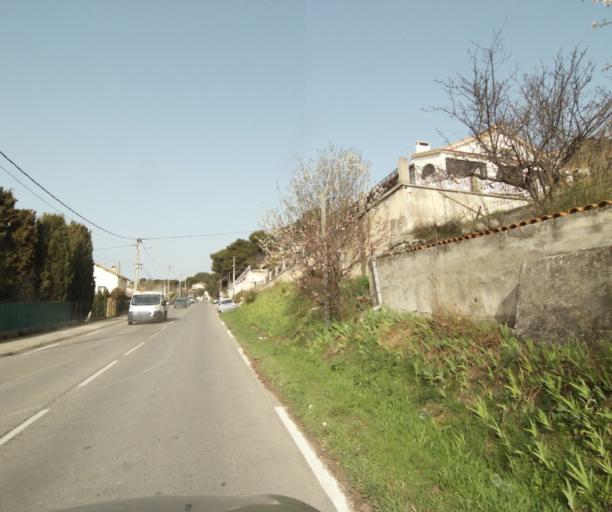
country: FR
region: Provence-Alpes-Cote d'Azur
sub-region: Departement des Bouches-du-Rhone
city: Marseille 15
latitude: 43.3916
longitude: 5.3439
